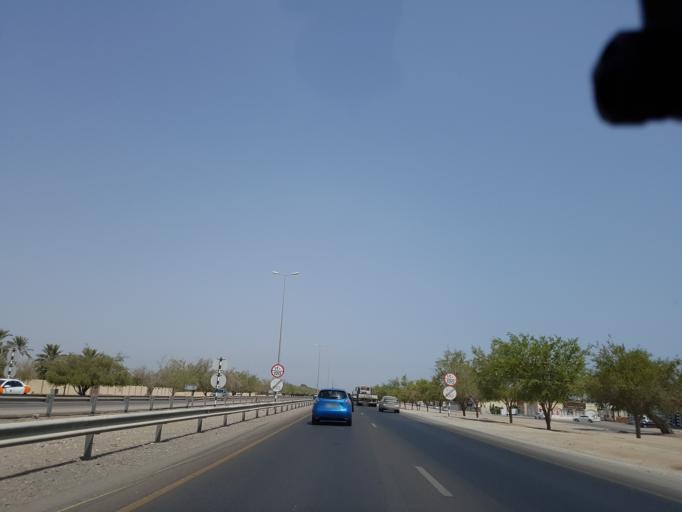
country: OM
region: Al Batinah
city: Saham
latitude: 24.1582
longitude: 56.8654
